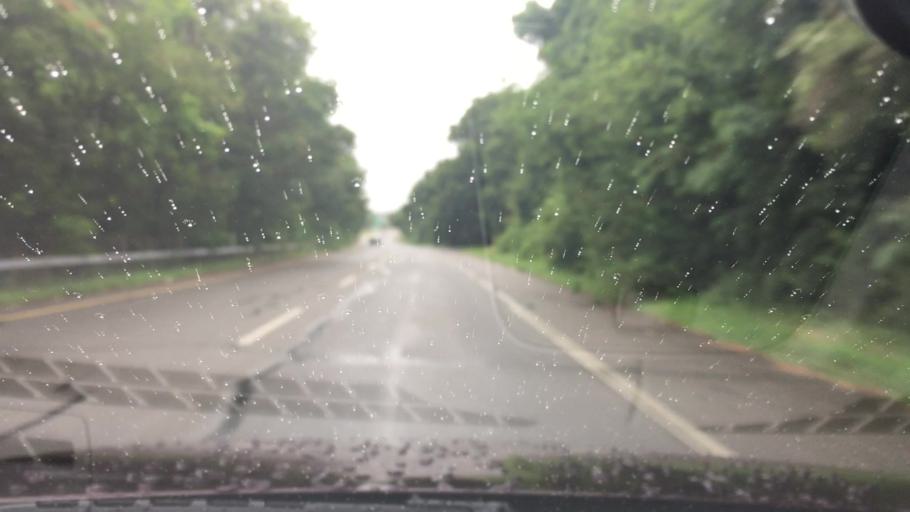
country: US
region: New York
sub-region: Suffolk County
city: Hauppauge
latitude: 40.8097
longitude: -73.2012
